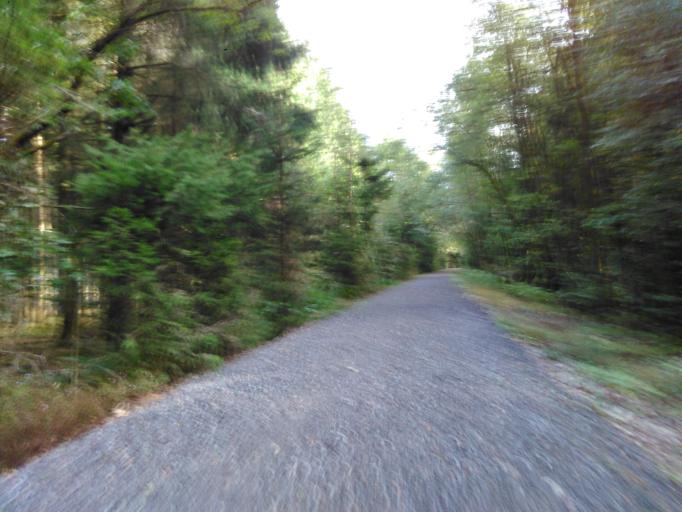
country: BE
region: Wallonia
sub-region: Province du Luxembourg
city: Vaux-sur-Sure
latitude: 49.9343
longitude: 5.5208
